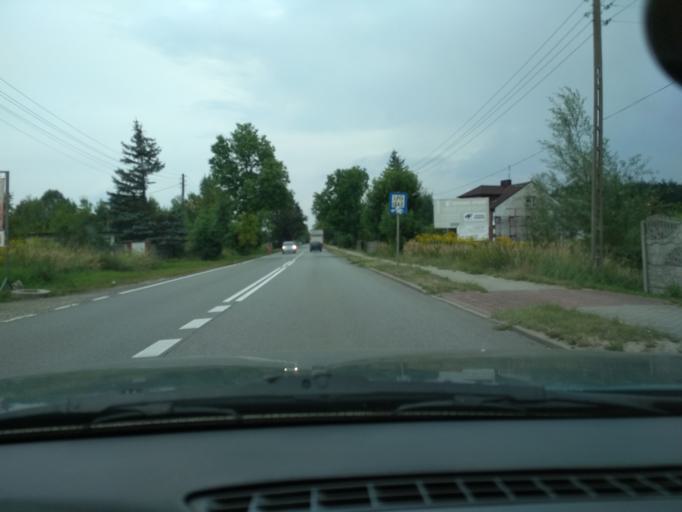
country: PL
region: Silesian Voivodeship
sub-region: Powiat zawiercianski
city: Wysoka
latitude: 50.4498
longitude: 19.3696
